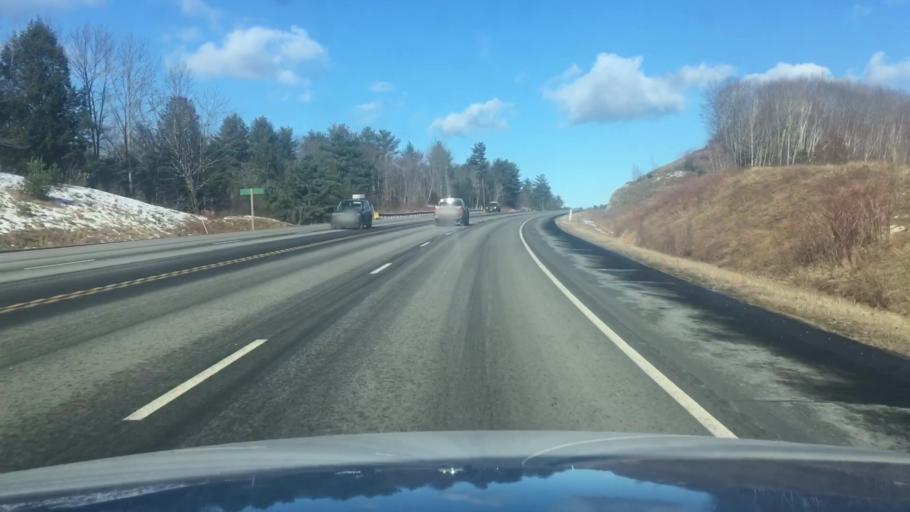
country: US
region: Maine
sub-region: Kennebec County
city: Augusta
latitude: 44.3372
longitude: -69.7663
